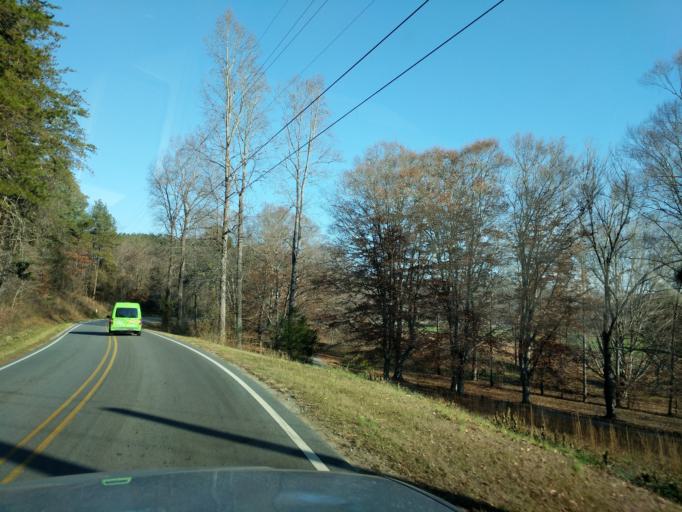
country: US
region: North Carolina
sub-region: Rutherford County
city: Rutherfordton
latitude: 35.2802
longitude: -82.0307
